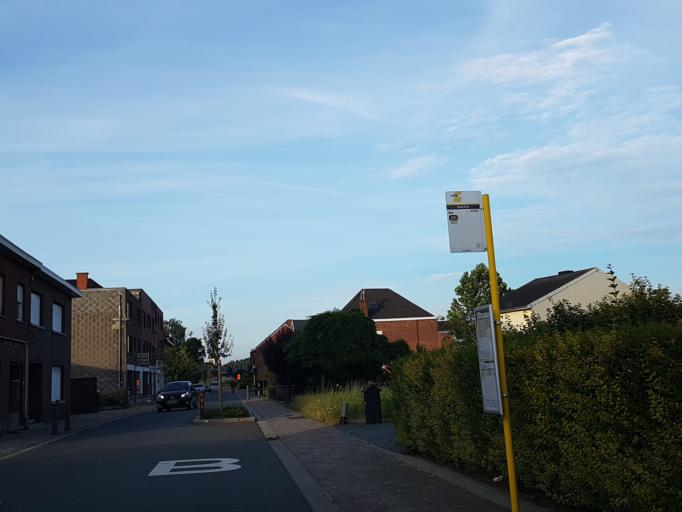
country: BE
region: Flanders
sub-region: Provincie Vlaams-Brabant
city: Londerzeel
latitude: 50.9933
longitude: 4.2615
